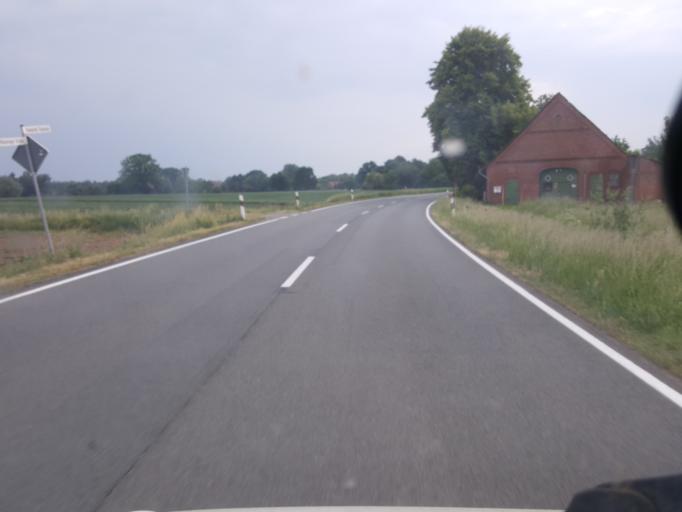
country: DE
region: Lower Saxony
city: Raddestorf
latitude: 52.4857
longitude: 9.0096
